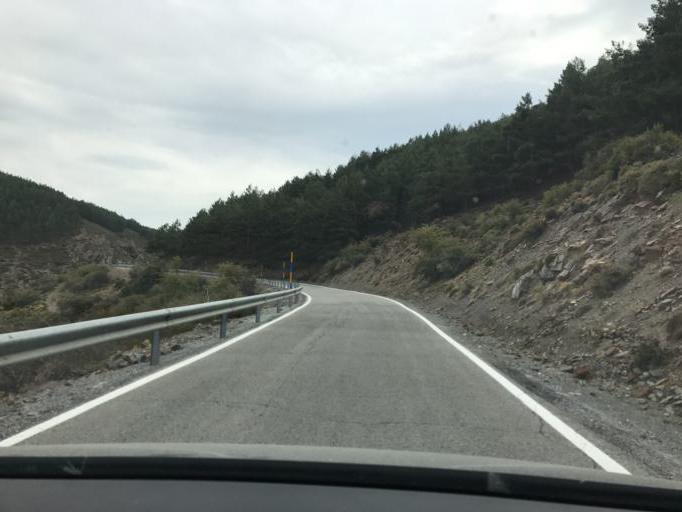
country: ES
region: Andalusia
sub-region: Provincia de Granada
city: Ferreira
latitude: 37.1233
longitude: -3.0355
